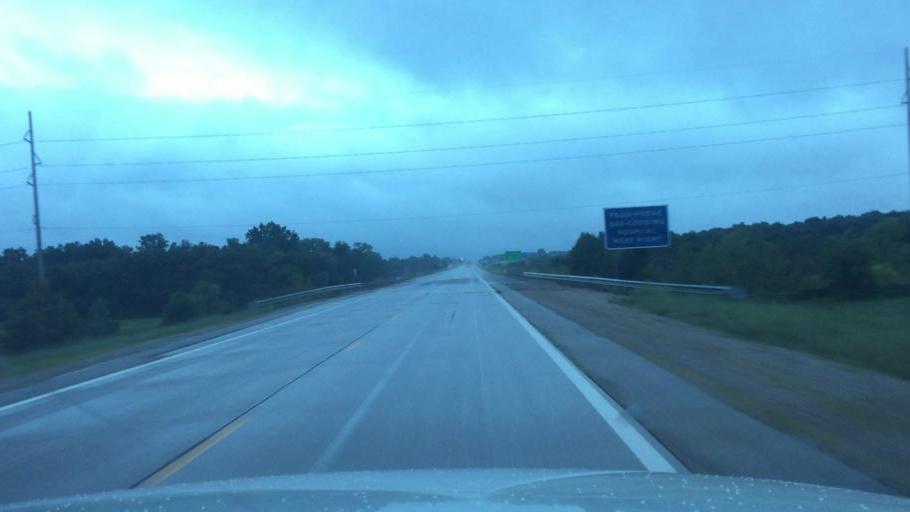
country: US
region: Kansas
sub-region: Neosho County
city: Chanute
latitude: 37.7044
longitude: -95.4795
